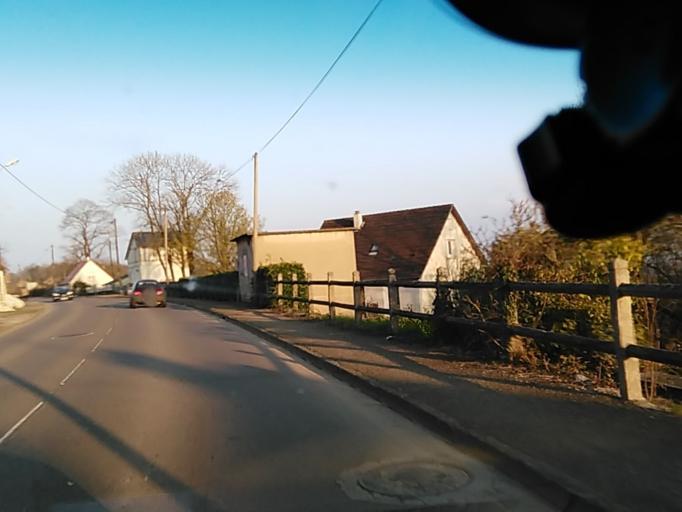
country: FR
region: Lower Normandy
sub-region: Departement de l'Orne
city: Domfront
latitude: 48.5912
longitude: -0.6366
